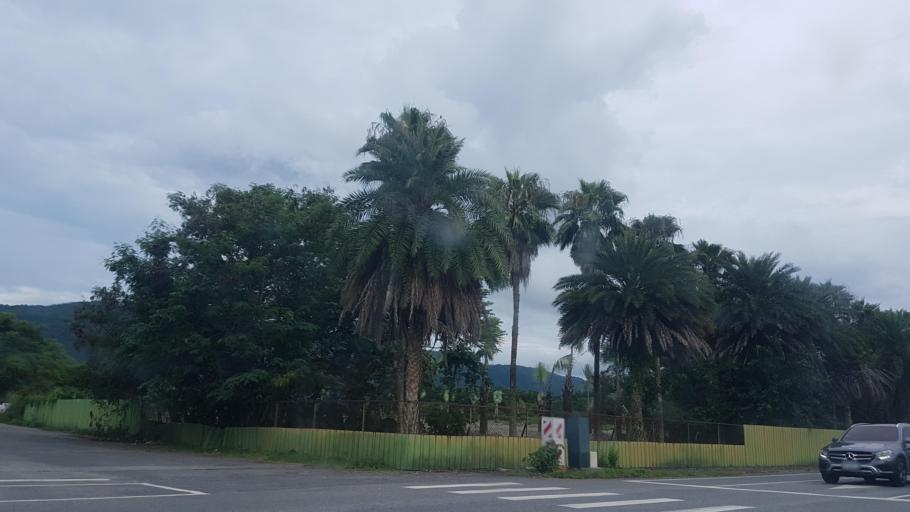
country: TW
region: Taiwan
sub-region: Hualien
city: Hualian
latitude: 23.8635
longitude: 121.5304
